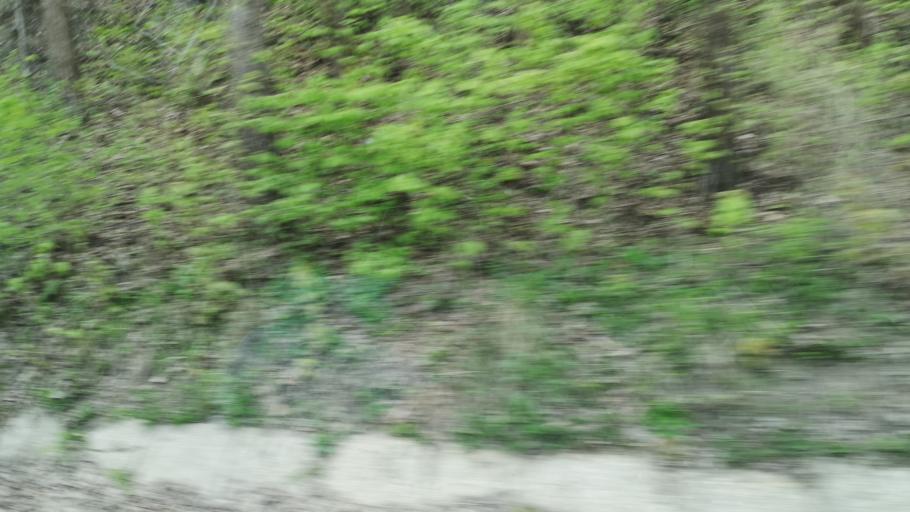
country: RO
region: Prahova
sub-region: Comuna Soimari
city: Soimari
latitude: 45.1610
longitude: 26.2053
